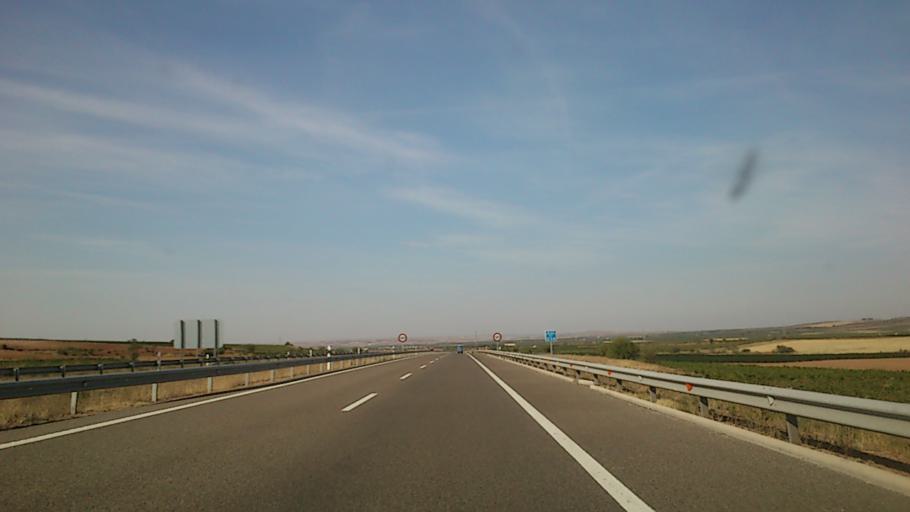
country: ES
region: Aragon
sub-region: Provincia de Zaragoza
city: Paniza
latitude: 41.3115
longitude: -1.2093
